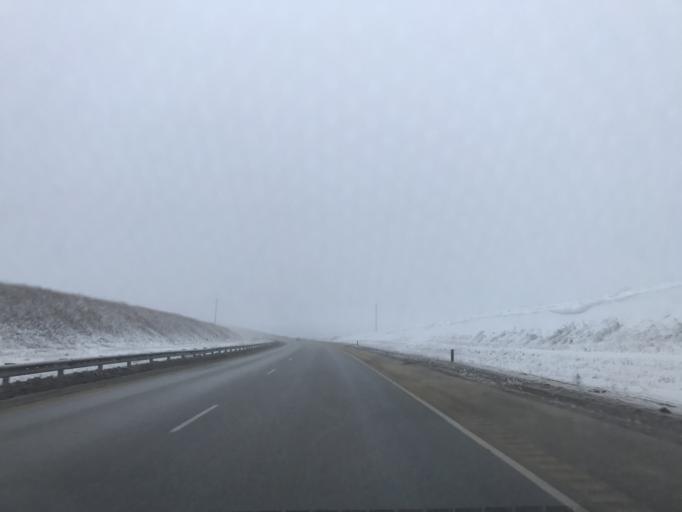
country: RU
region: Rostov
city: Temernik
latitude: 47.3656
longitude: 39.7631
